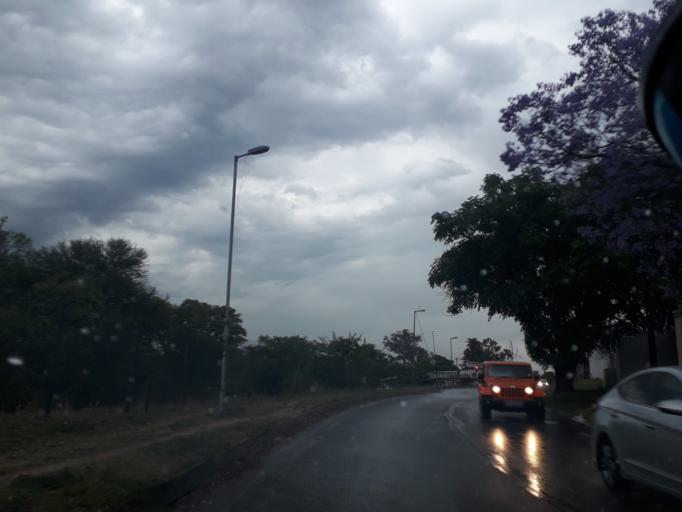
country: ZA
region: Gauteng
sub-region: City of Johannesburg Metropolitan Municipality
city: Johannesburg
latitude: -26.0796
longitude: 27.9873
